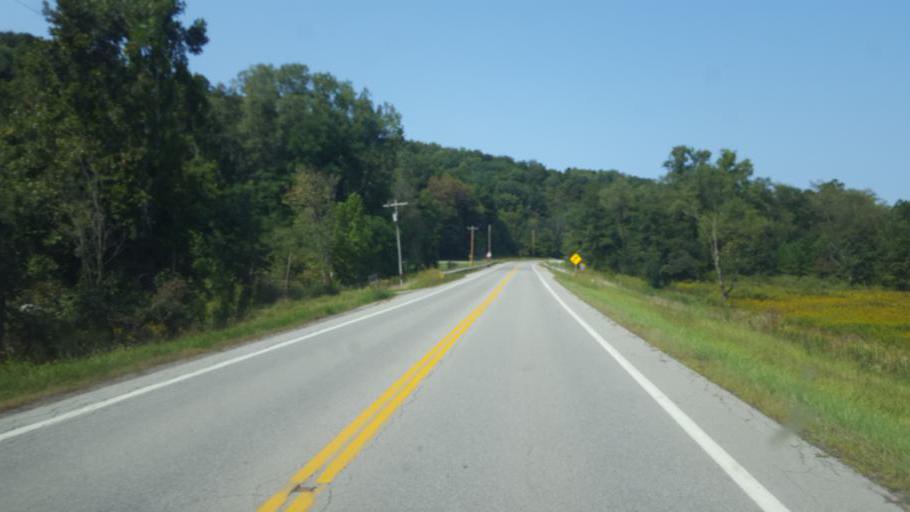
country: US
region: Ohio
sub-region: Ashland County
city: Loudonville
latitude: 40.5944
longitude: -82.2655
